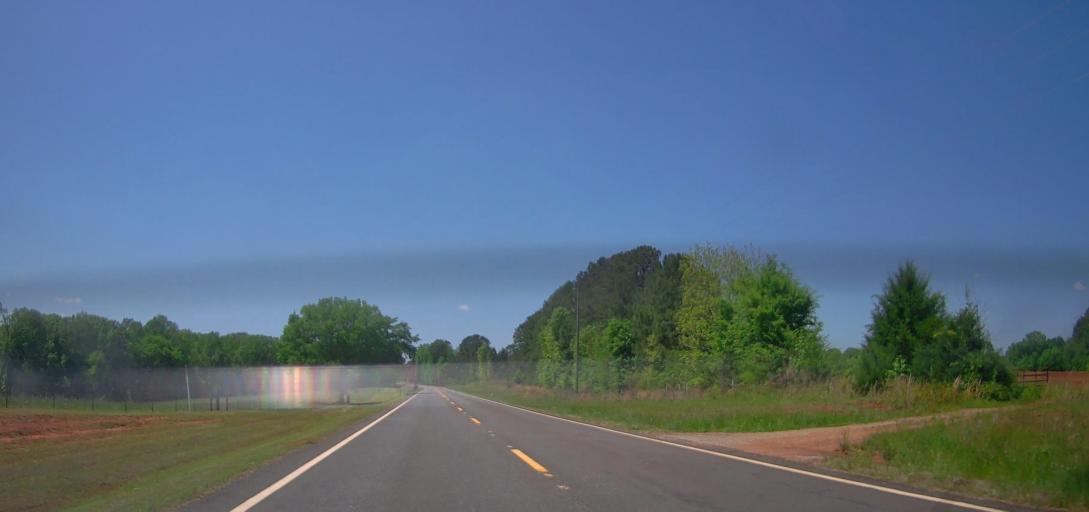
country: US
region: Georgia
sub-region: Jasper County
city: Monticello
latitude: 33.2883
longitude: -83.6308
